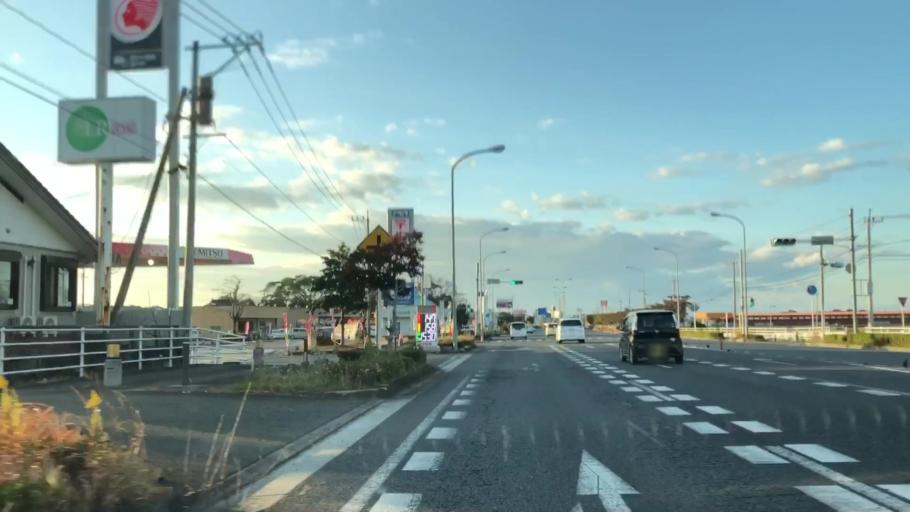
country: JP
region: Fukuoka
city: Nakatsu
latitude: 33.5480
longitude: 131.2791
